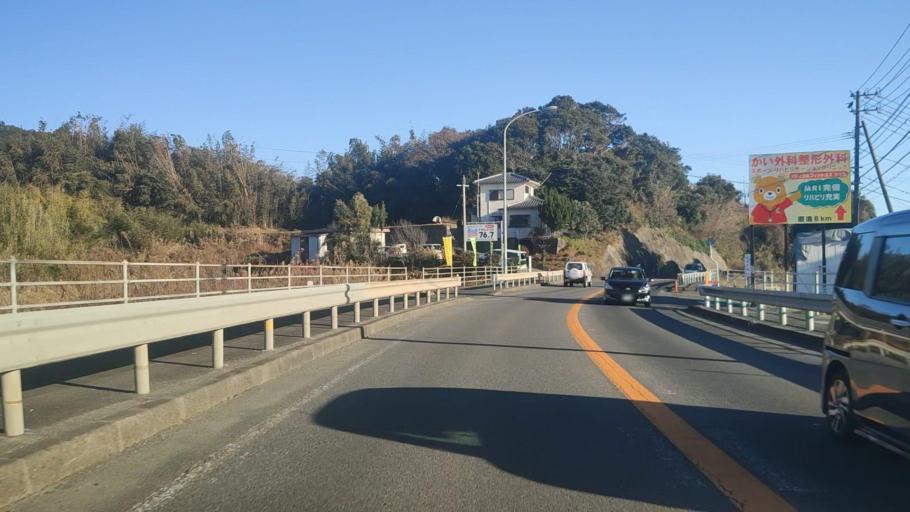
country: JP
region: Miyazaki
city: Nobeoka
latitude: 32.3642
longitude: 131.6233
